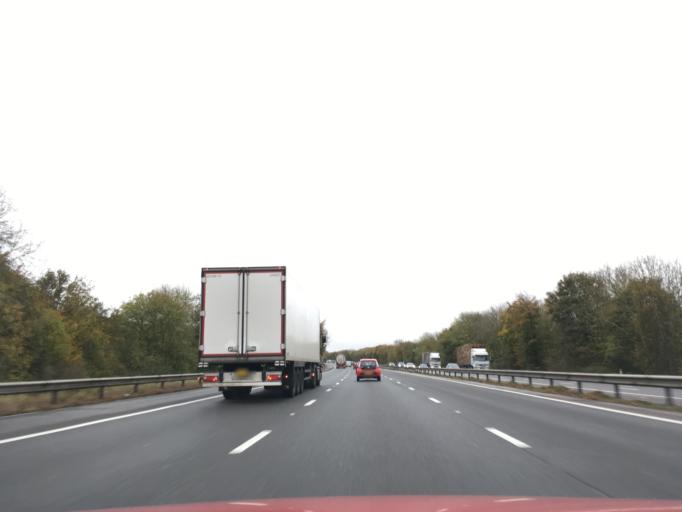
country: GB
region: England
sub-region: Borough of Swindon
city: Bishopstone
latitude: 51.5168
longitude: -1.6526
